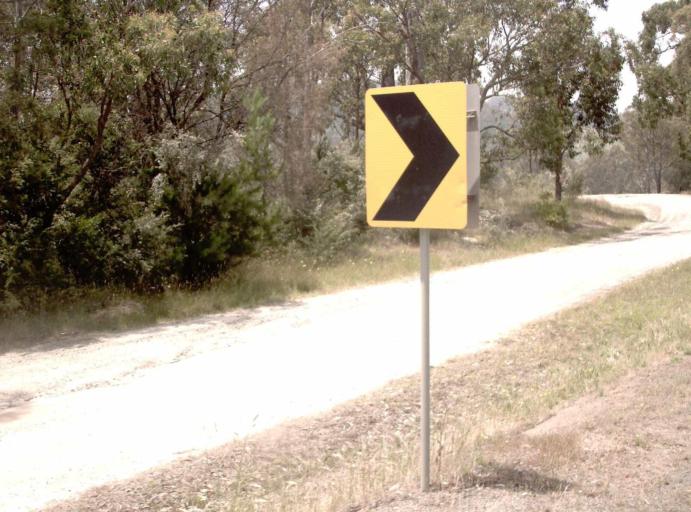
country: AU
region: Victoria
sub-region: Latrobe
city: Traralgon
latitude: -38.3173
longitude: 146.7209
